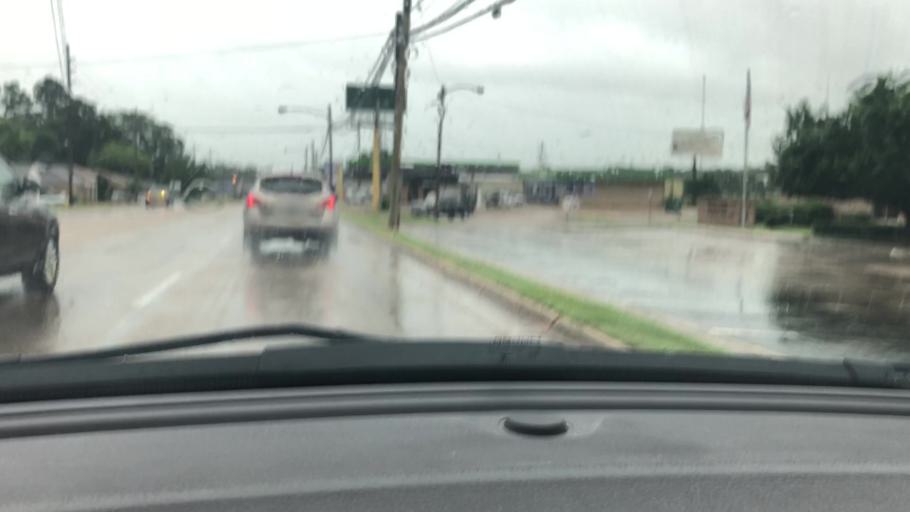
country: US
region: Texas
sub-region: Bowie County
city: Wake Village
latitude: 33.4395
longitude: -94.0804
